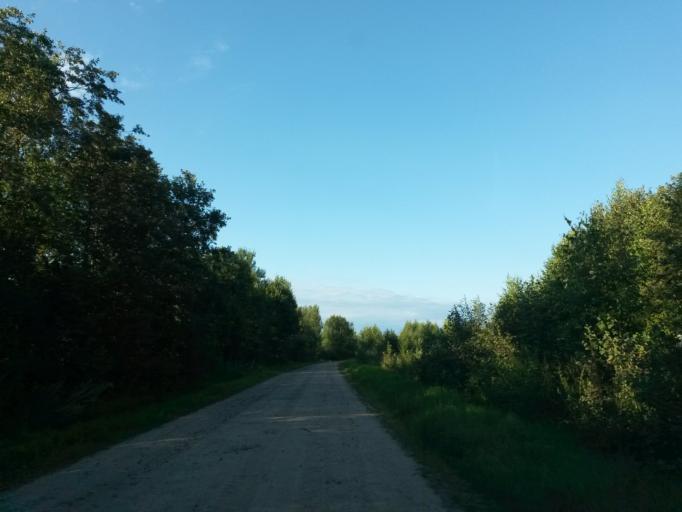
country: RU
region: Jaroslavl
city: Tutayev
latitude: 57.9437
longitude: 39.4486
